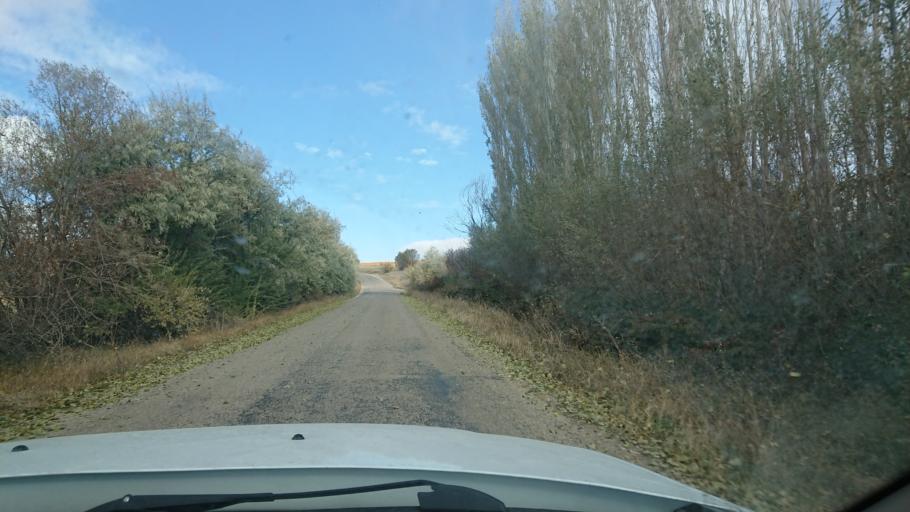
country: TR
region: Aksaray
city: Agacoren
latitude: 38.8321
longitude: 33.9559
